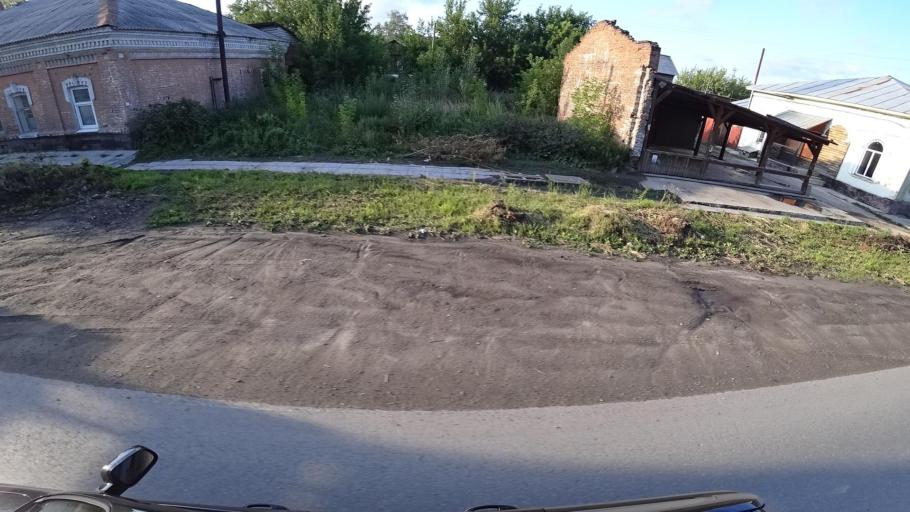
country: RU
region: Sverdlovsk
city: Kamyshlov
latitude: 56.8472
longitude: 62.7065
